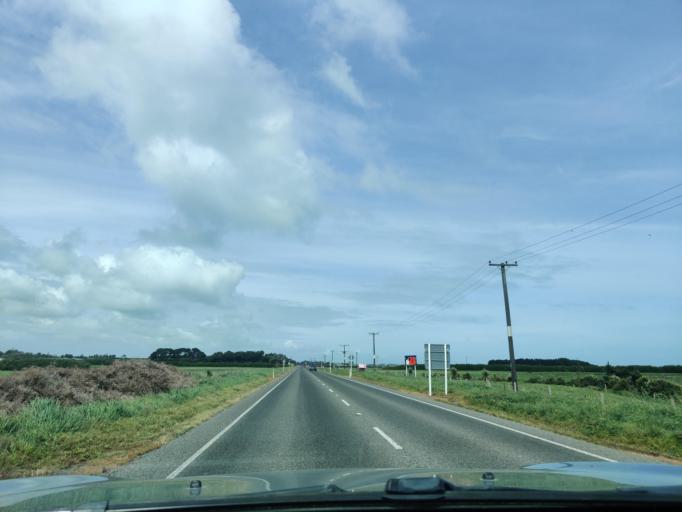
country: NZ
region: Taranaki
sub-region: South Taranaki District
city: Hawera
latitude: -39.5778
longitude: 174.2206
